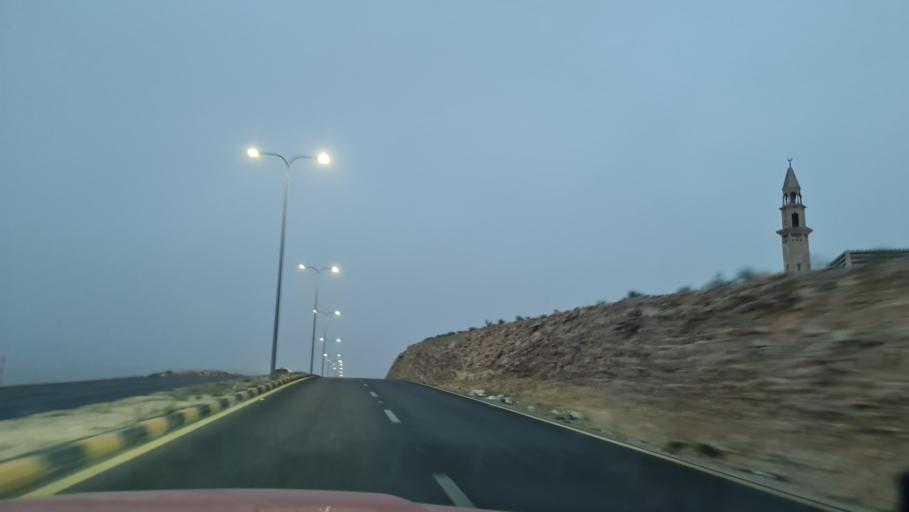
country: JO
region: Zarqa
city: Zarqa
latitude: 32.0476
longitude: 36.1057
